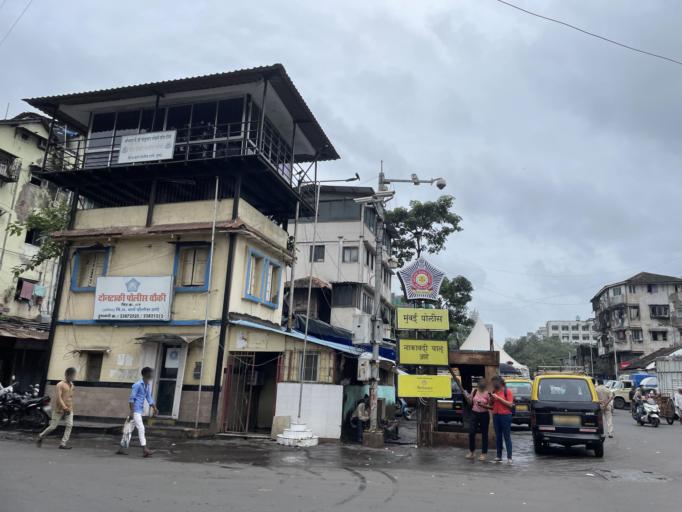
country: IN
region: Maharashtra
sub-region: Mumbai Suburban
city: Mumbai
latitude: 18.9617
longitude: 72.8286
